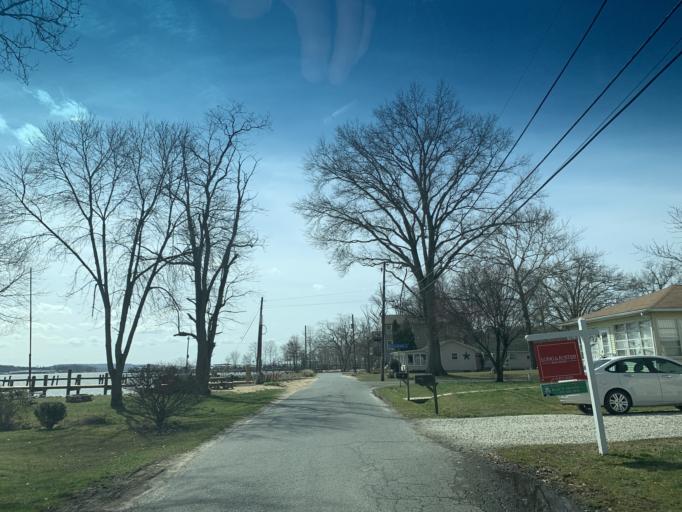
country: US
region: Maryland
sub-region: Cecil County
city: Charlestown
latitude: 39.5778
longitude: -75.9668
